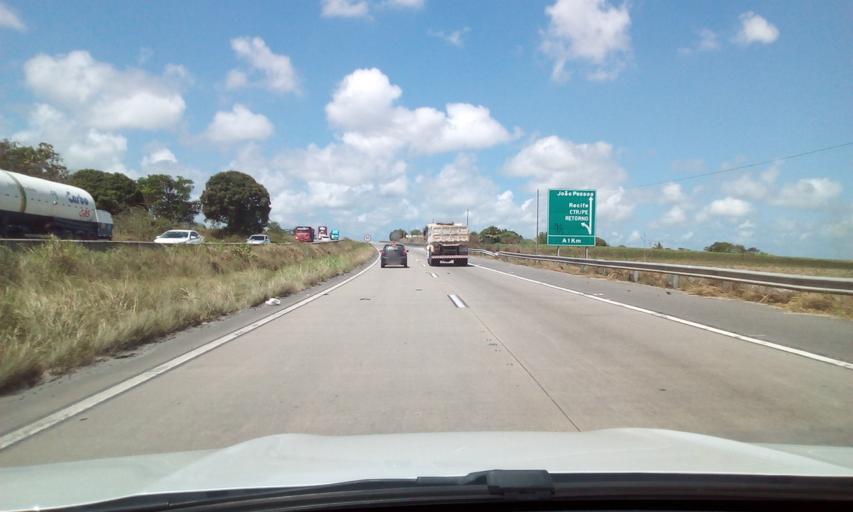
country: BR
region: Pernambuco
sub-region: Itapissuma
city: Itapissuma
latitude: -7.7078
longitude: -34.9276
